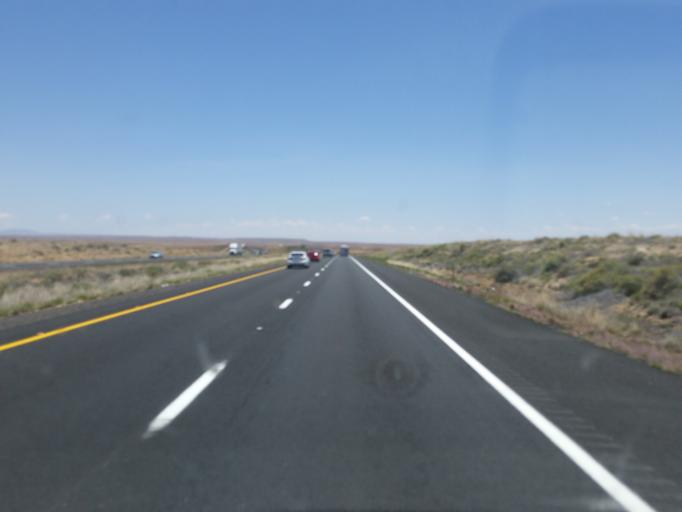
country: US
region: Arizona
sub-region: Coconino County
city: LeChee
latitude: 35.1013
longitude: -110.9856
